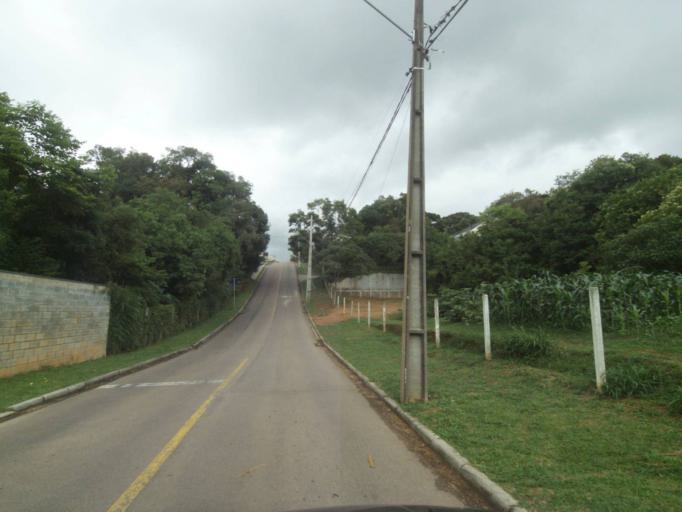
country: BR
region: Parana
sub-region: Curitiba
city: Curitiba
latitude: -25.4465
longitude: -49.3339
